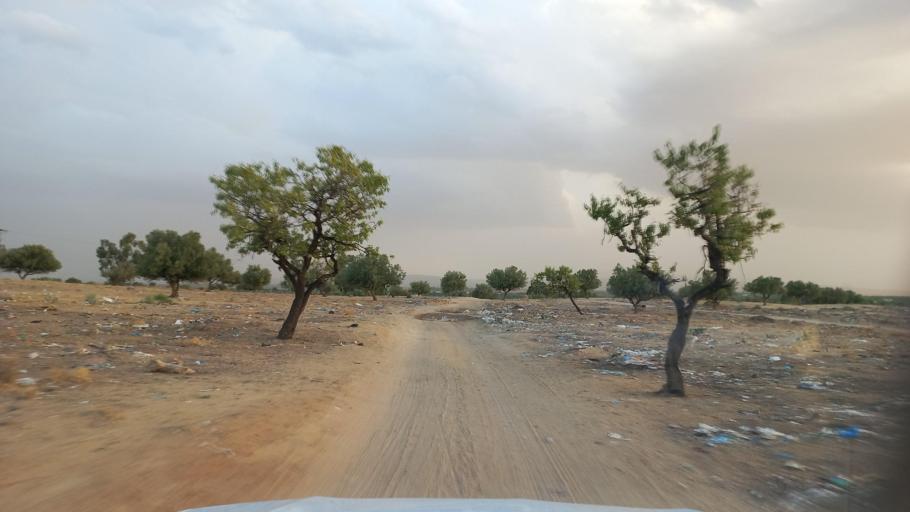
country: TN
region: Al Qasrayn
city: Kasserine
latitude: 35.2709
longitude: 9.0720
